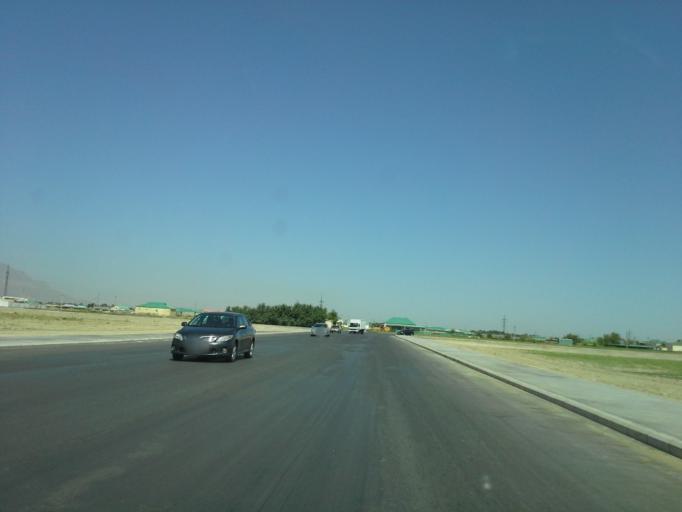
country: TM
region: Ahal
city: Ashgabat
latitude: 37.9802
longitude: 58.3244
